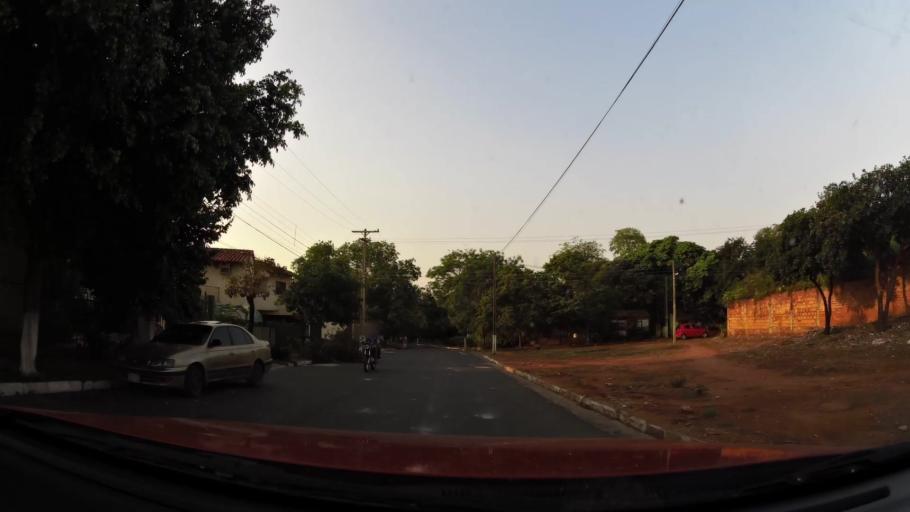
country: PY
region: Central
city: Lambare
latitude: -25.3536
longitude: -57.6040
